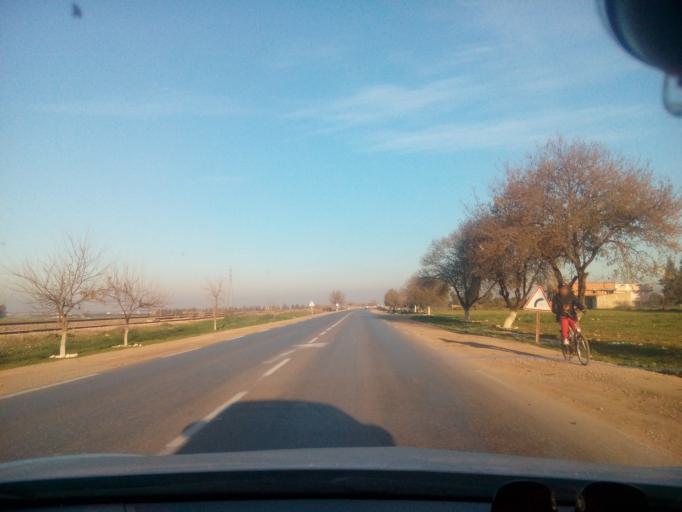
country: DZ
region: Chlef
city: Boukadir
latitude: 36.0495
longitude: 1.0894
